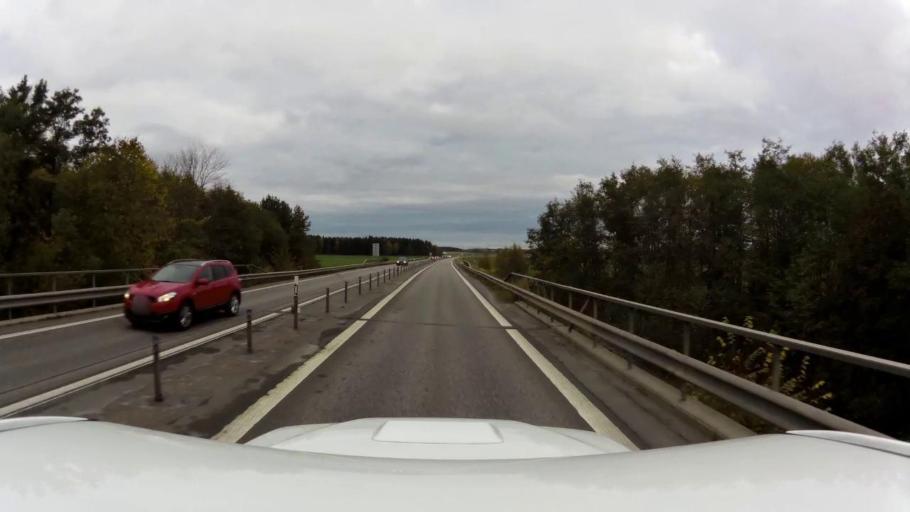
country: SE
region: OEstergoetland
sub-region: Linkopings Kommun
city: Berg
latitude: 58.4533
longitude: 15.5038
